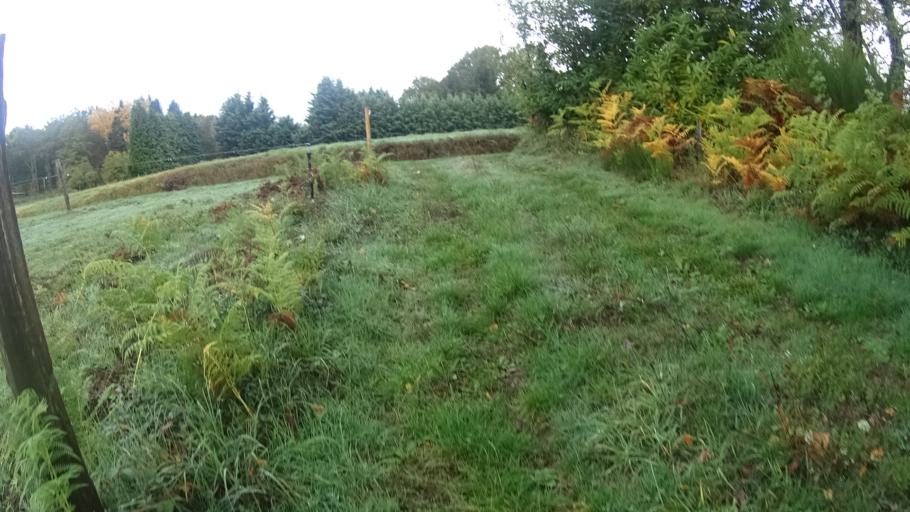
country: FR
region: Aquitaine
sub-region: Departement de la Dordogne
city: Payzac
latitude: 45.3592
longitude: 1.2058
